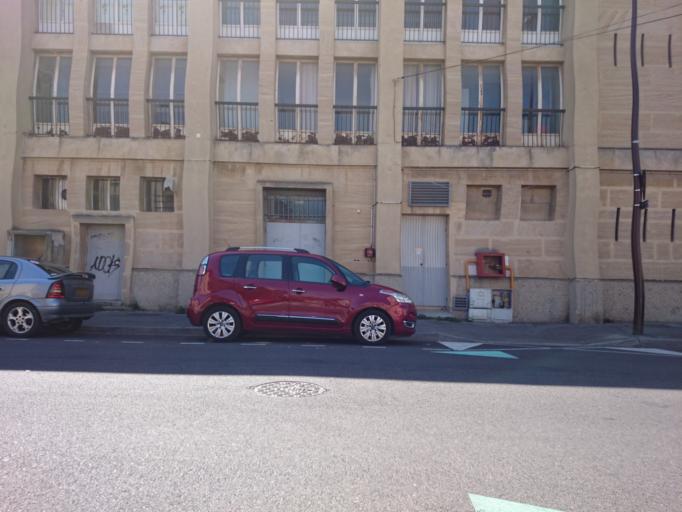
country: FR
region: Provence-Alpes-Cote d'Azur
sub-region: Departement du Vaucluse
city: Avignon
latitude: 43.9406
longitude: 4.8010
